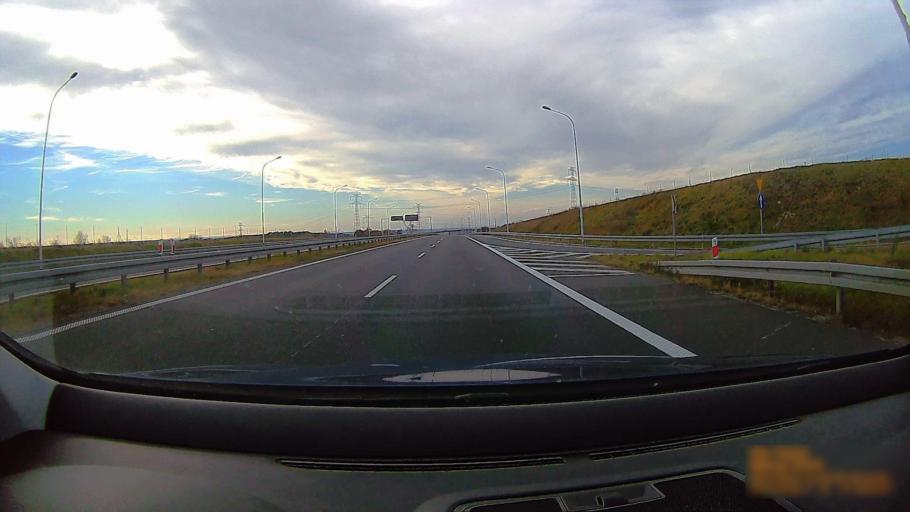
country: PL
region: Greater Poland Voivodeship
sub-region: Powiat ostrowski
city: Przygodzice
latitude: 51.6288
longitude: 17.8676
